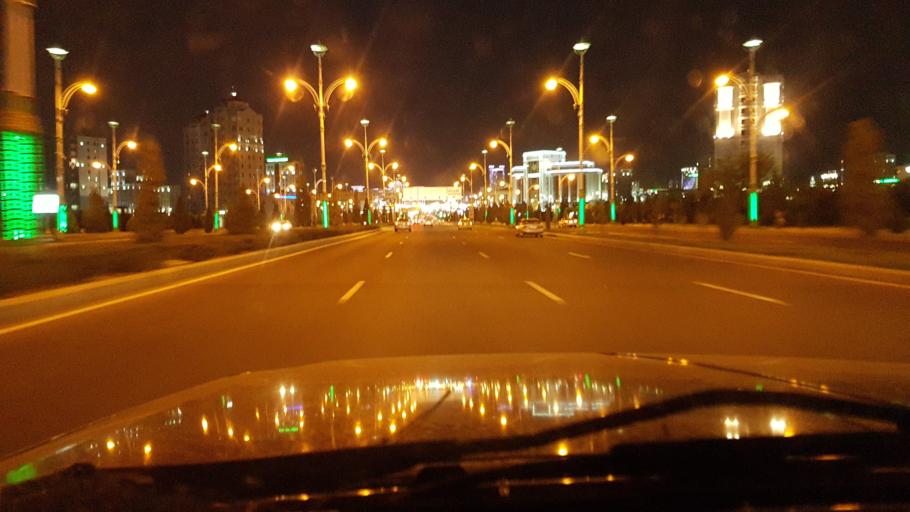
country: TM
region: Ahal
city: Ashgabat
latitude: 37.8993
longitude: 58.3555
